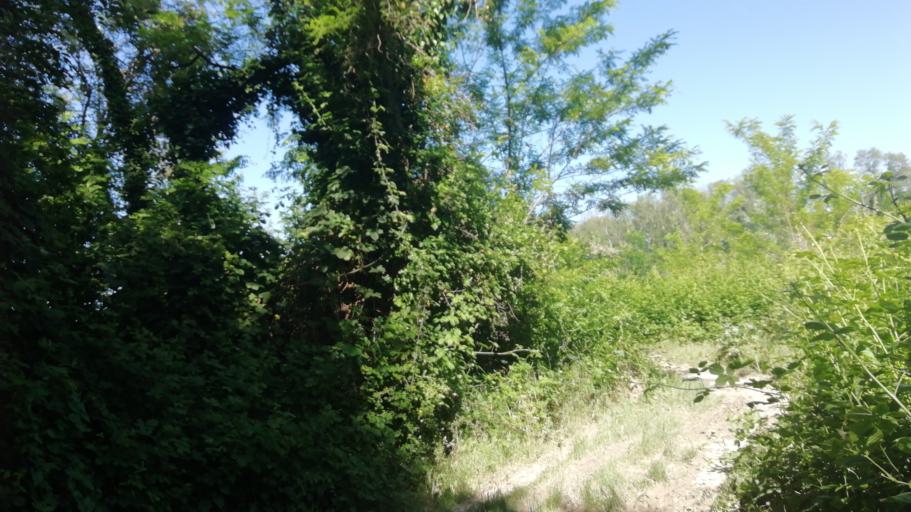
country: IT
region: Emilia-Romagna
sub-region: Provincia di Piacenza
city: Borgonovo Valtidone
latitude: 44.9811
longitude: 9.4619
